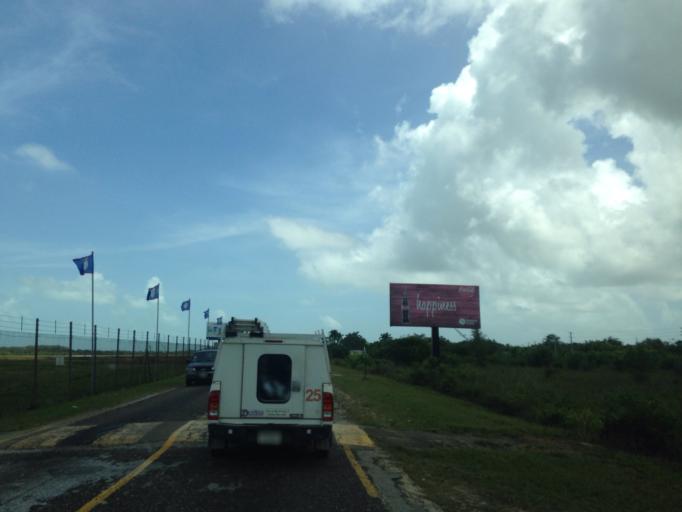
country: BZ
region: Belize
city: Belize City
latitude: 17.5376
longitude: -88.3046
